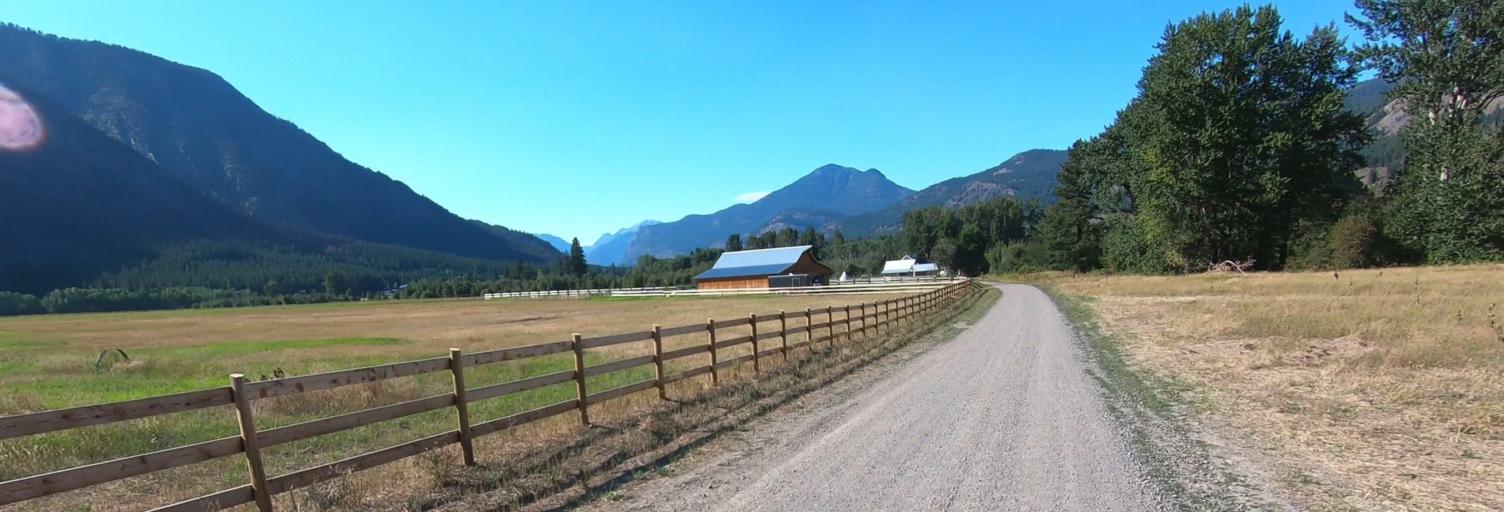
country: US
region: Washington
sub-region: Chelan County
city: Granite Falls
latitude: 48.5305
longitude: -120.3259
